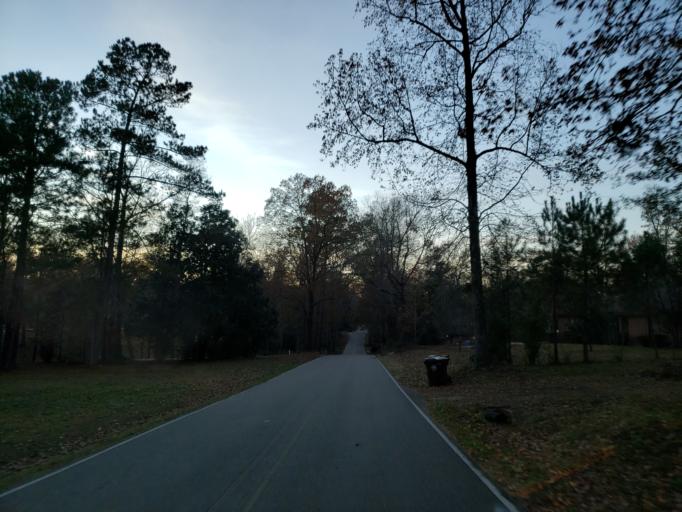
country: US
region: Mississippi
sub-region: Forrest County
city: Hattiesburg
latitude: 31.2445
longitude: -89.3209
